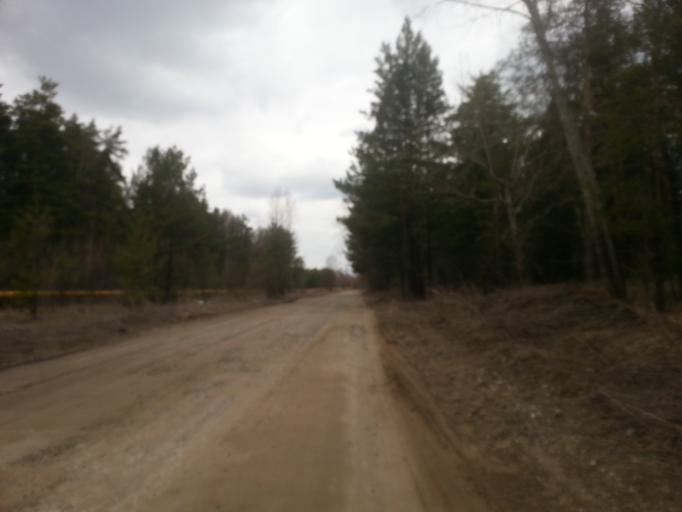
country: RU
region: Altai Krai
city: Yuzhnyy
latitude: 53.2826
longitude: 83.7332
